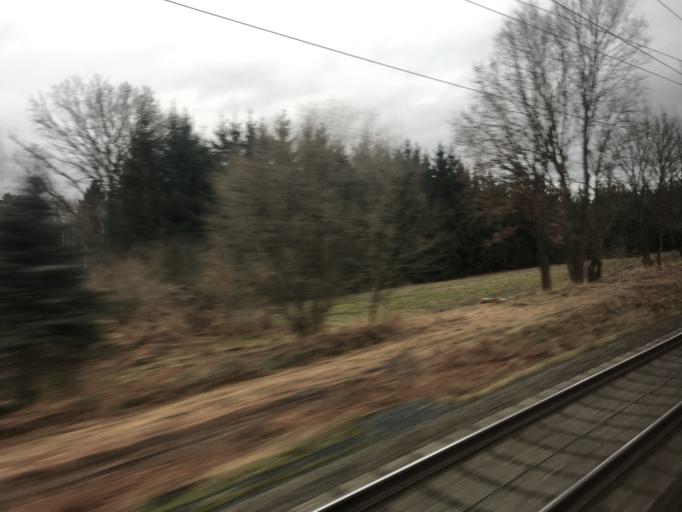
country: DE
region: Lower Saxony
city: Edemissen
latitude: 52.4359
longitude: 10.2531
